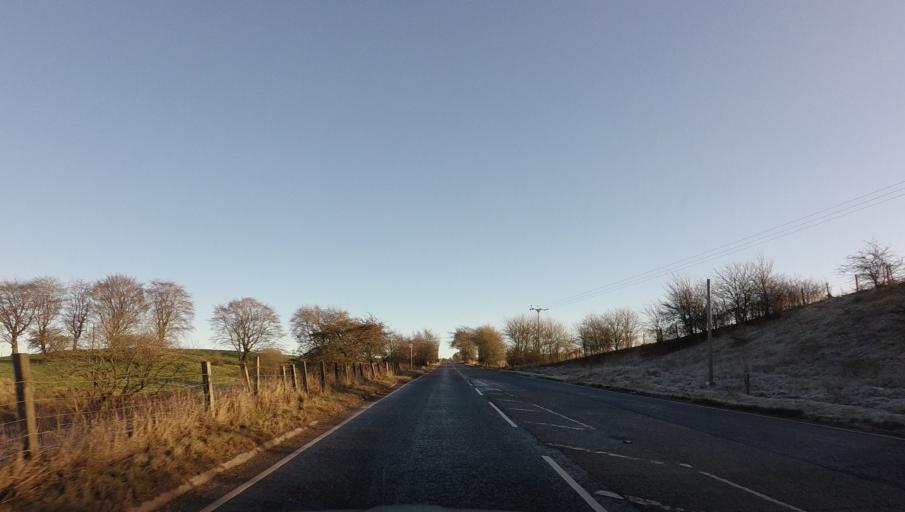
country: GB
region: Scotland
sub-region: North Lanarkshire
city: Shotts
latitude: 55.8078
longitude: -3.8066
